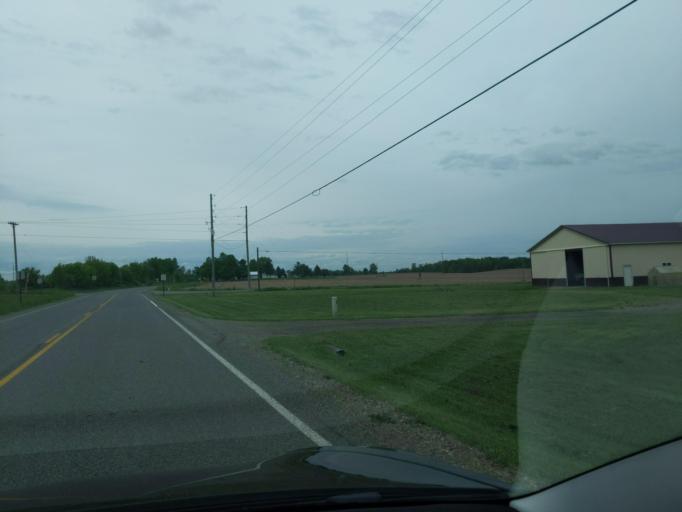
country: US
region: Michigan
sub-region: Ingham County
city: Leslie
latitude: 42.5085
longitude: -84.4279
